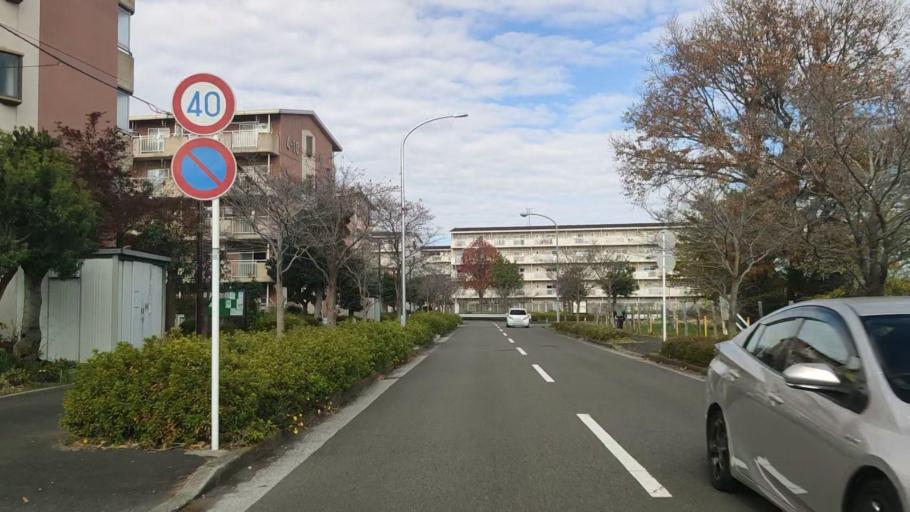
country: JP
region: Kanagawa
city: Minami-rinkan
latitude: 35.4820
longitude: 139.4906
